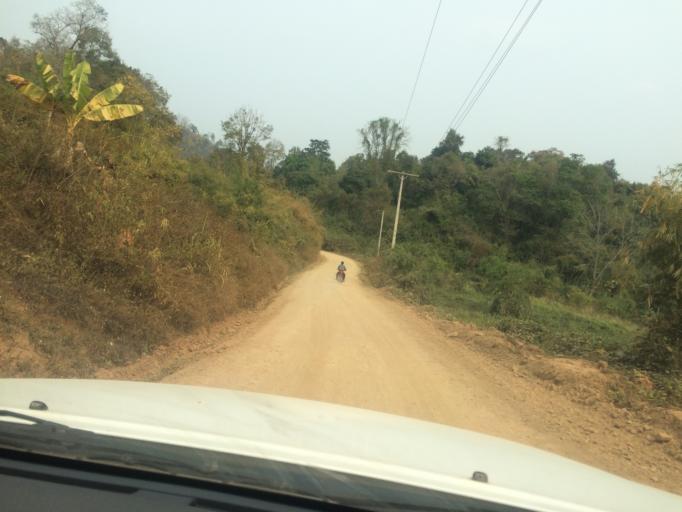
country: LA
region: Loungnamtha
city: Muang Nale
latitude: 20.4296
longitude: 101.7070
